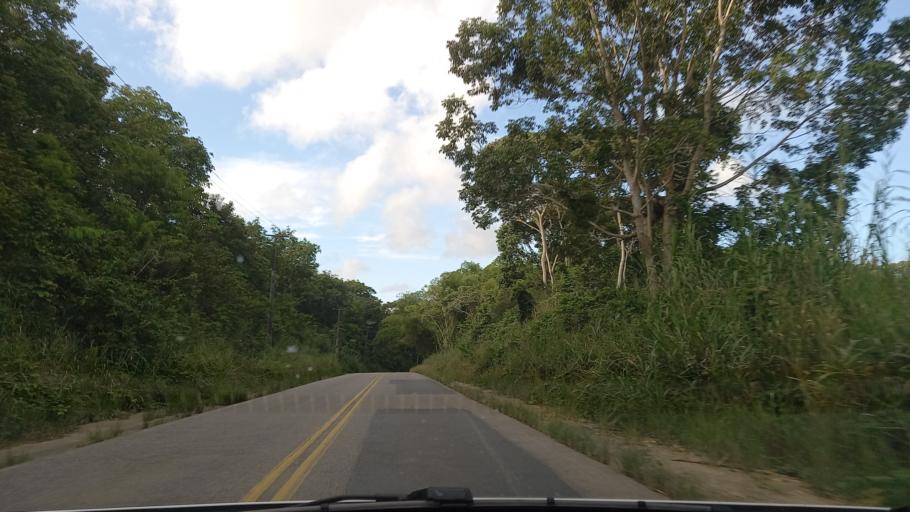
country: BR
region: Pernambuco
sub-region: Rio Formoso
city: Rio Formoso
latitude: -8.6505
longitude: -35.1314
